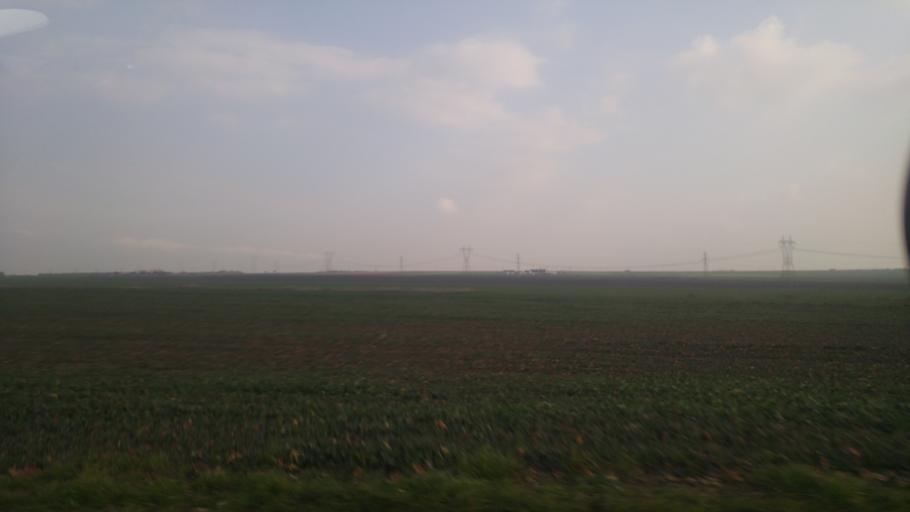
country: TR
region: Istanbul
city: Kavakli
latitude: 41.1019
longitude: 28.2850
